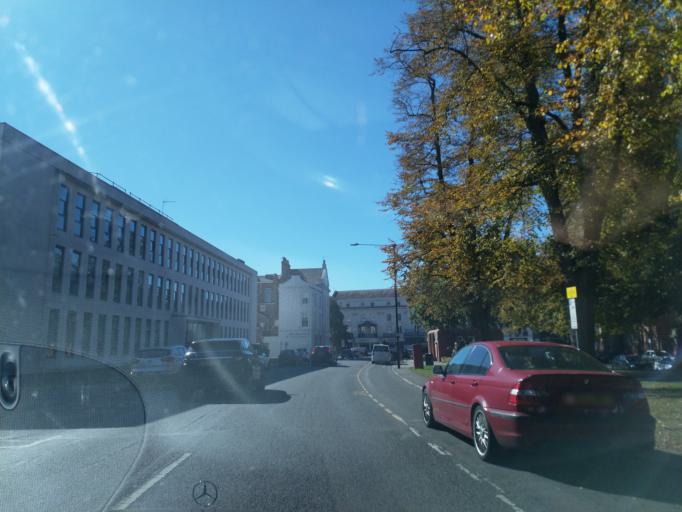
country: GB
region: England
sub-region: Warwickshire
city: Royal Leamington Spa
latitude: 52.2892
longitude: -1.5335
